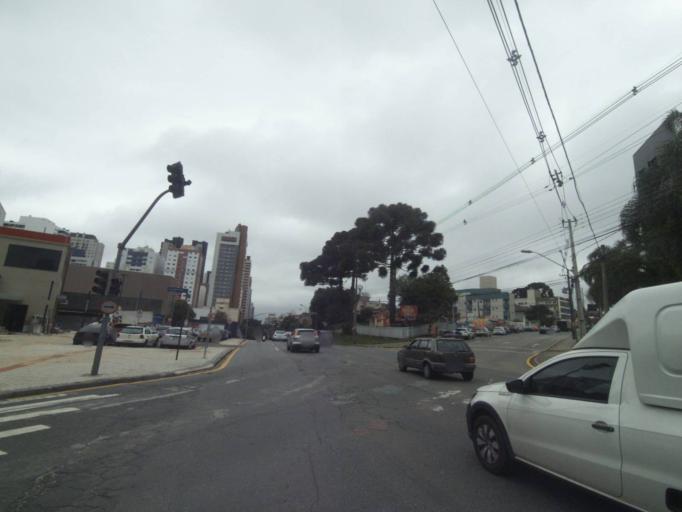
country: BR
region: Parana
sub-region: Curitiba
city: Curitiba
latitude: -25.4364
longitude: -49.3055
